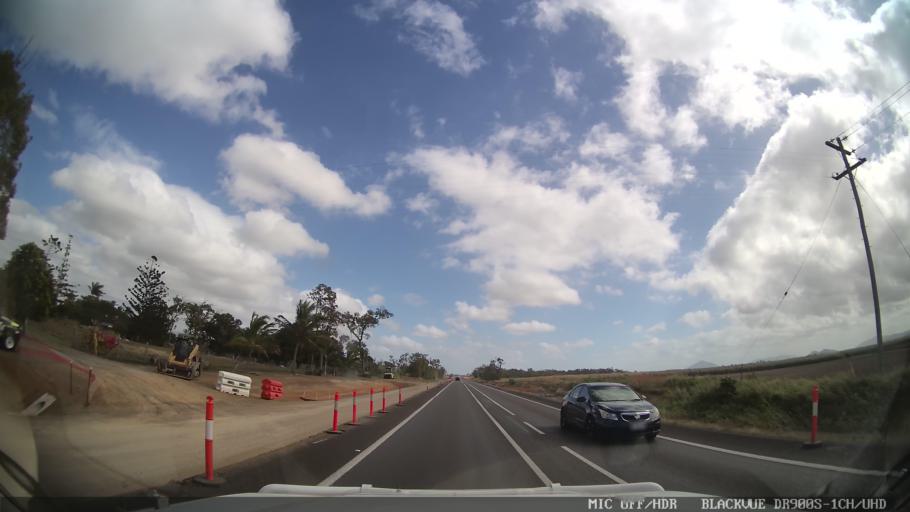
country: AU
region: Queensland
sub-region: Whitsunday
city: Red Hill
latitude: -20.2983
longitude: 148.5080
